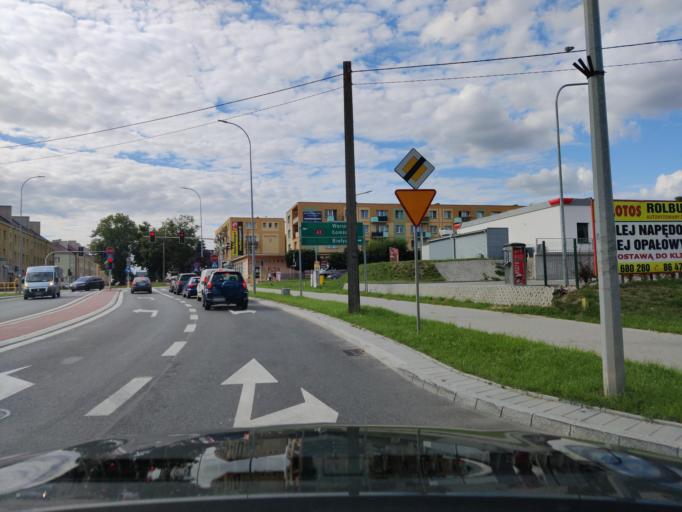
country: PL
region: Podlasie
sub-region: Powiat zambrowski
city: Zambrow
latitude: 52.9860
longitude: 22.2450
